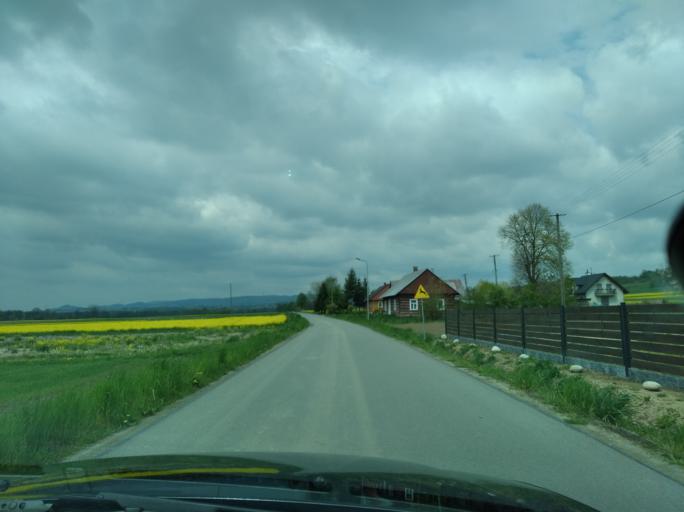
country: PL
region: Subcarpathian Voivodeship
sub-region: Powiat brzozowski
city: Jablonica Polska
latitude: 49.6796
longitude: 21.9006
